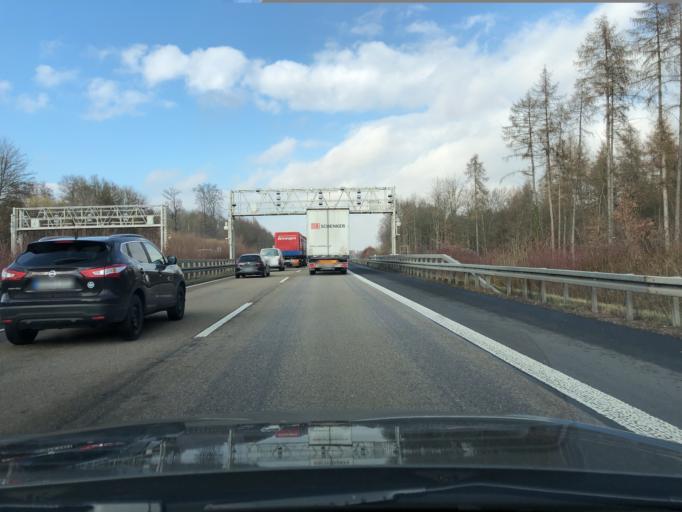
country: DE
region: Hesse
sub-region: Regierungsbezirk Darmstadt
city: Hammersbach
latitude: 50.2056
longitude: 9.0013
